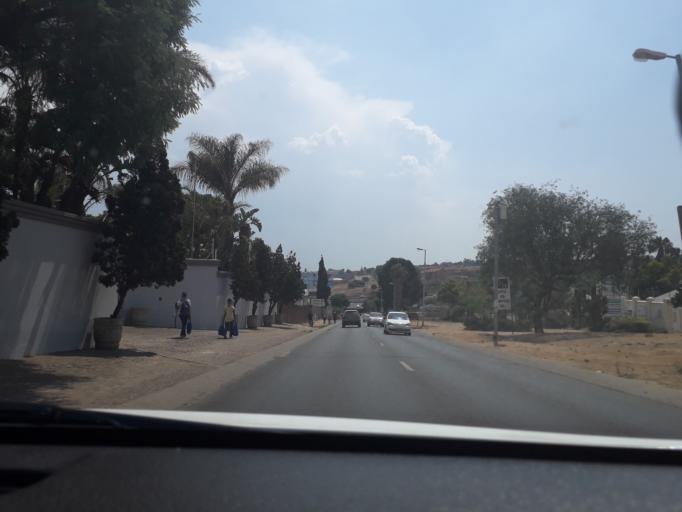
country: ZA
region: Gauteng
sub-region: City of Johannesburg Metropolitan Municipality
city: Midrand
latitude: -25.9941
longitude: 28.1255
